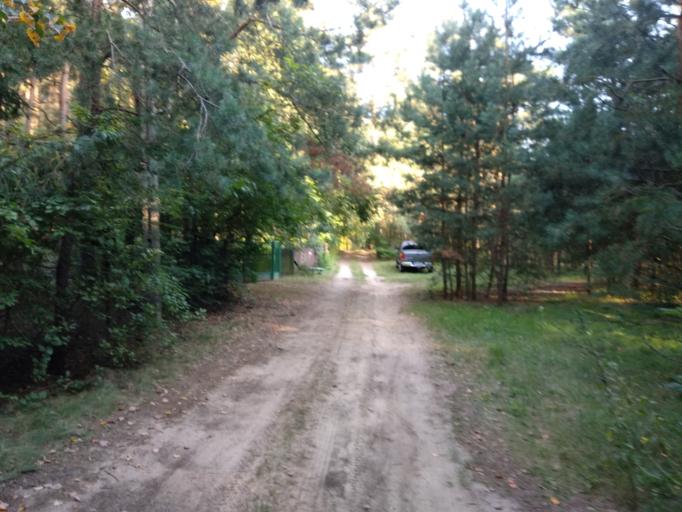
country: PL
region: Masovian Voivodeship
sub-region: Powiat pultuski
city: Obryte
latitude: 52.7551
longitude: 21.1980
